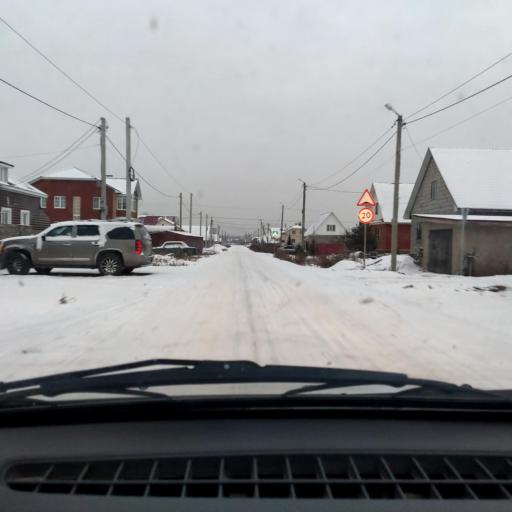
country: RU
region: Bashkortostan
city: Mikhaylovka
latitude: 54.7920
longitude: 55.8263
